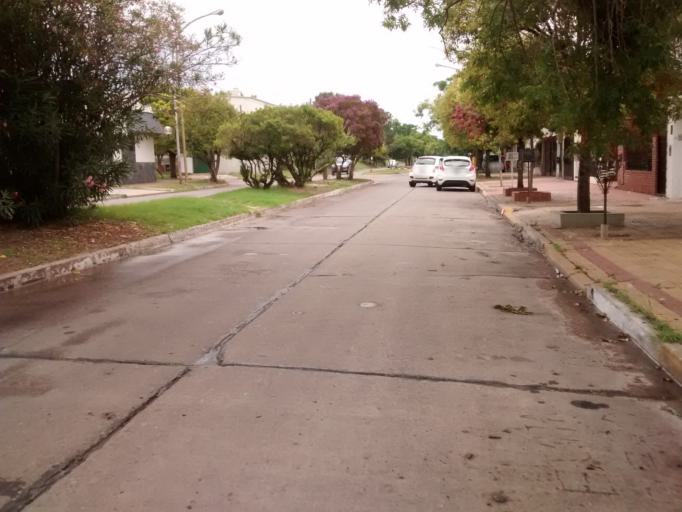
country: AR
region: Buenos Aires
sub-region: Partido de La Plata
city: La Plata
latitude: -34.8959
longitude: -57.9715
